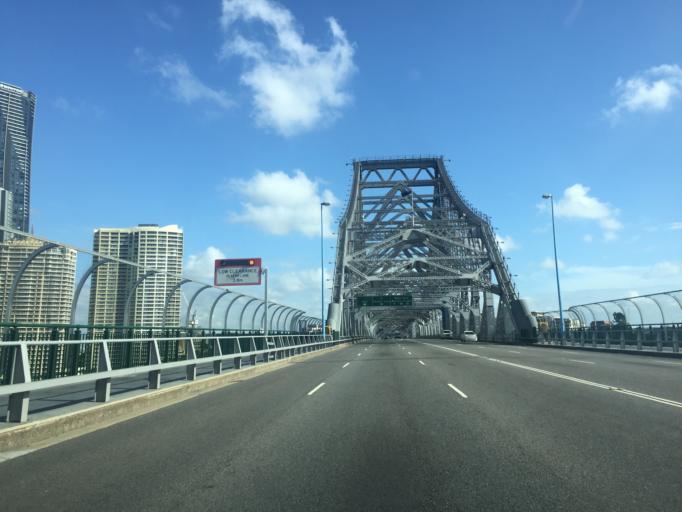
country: AU
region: Queensland
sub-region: Brisbane
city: Brisbane
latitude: -27.4663
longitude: 153.0358
